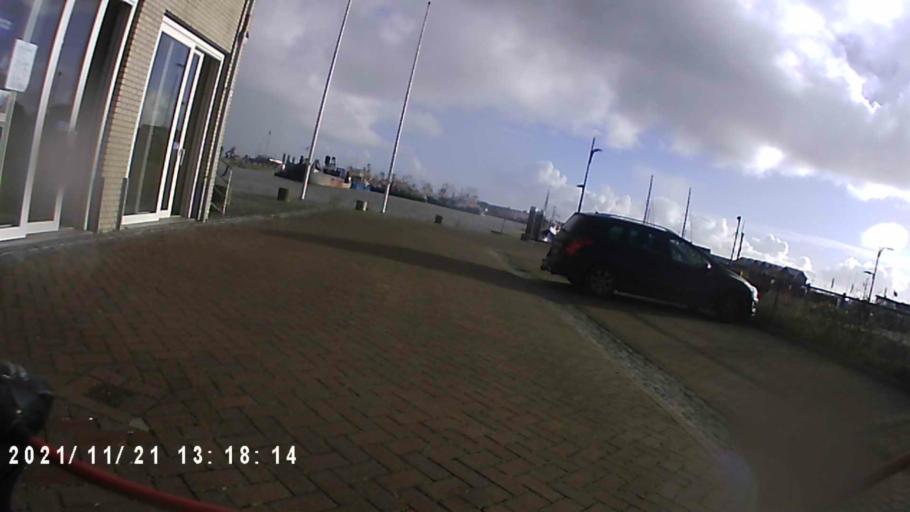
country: NL
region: Friesland
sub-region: Gemeente Dongeradeel
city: Anjum
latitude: 53.4089
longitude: 6.1984
